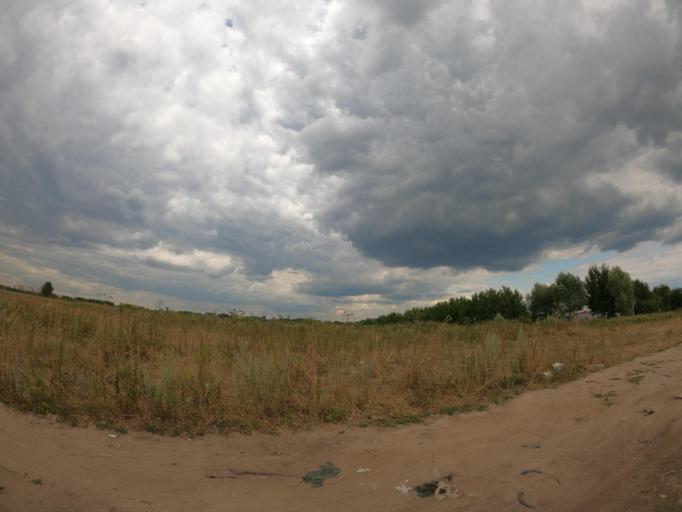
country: RU
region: Moskovskaya
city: Ramenskoye
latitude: 55.5424
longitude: 38.2235
